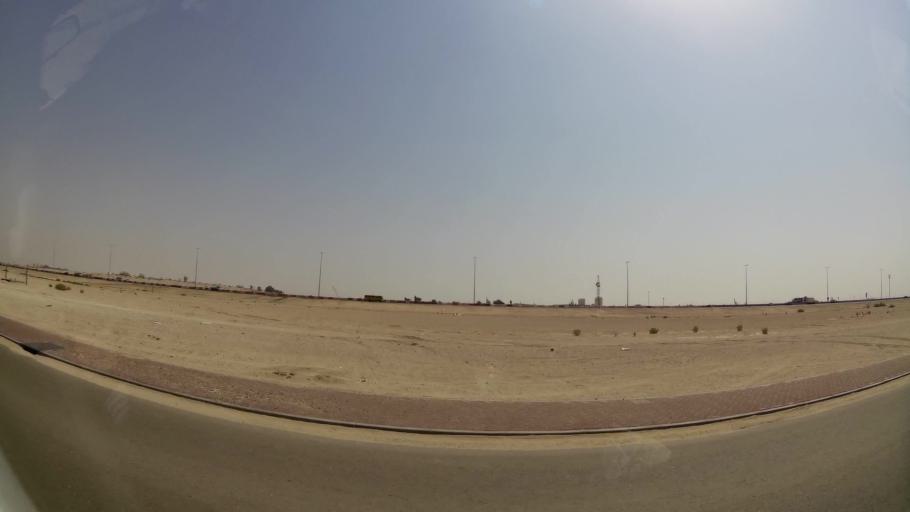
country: AE
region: Abu Dhabi
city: Abu Dhabi
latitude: 24.3001
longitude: 54.5828
